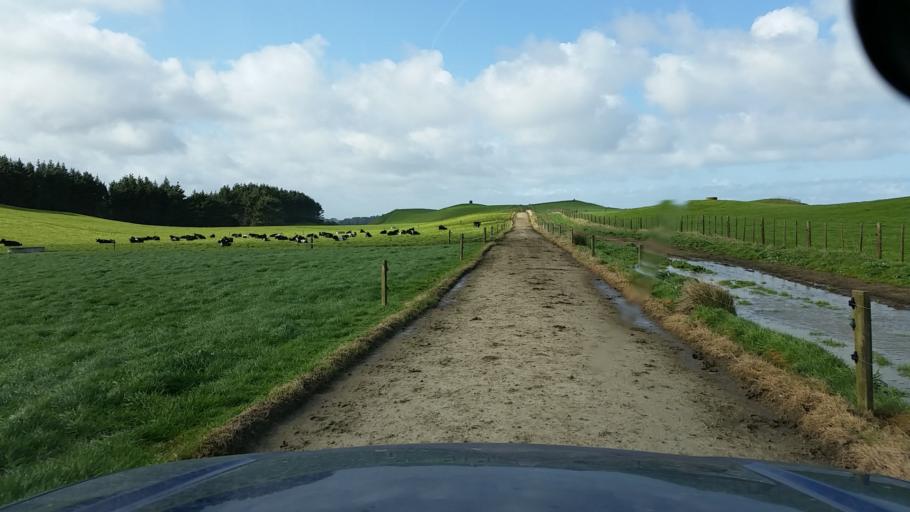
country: NZ
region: Taranaki
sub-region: South Taranaki District
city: Patea
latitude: -39.7438
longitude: 174.5342
